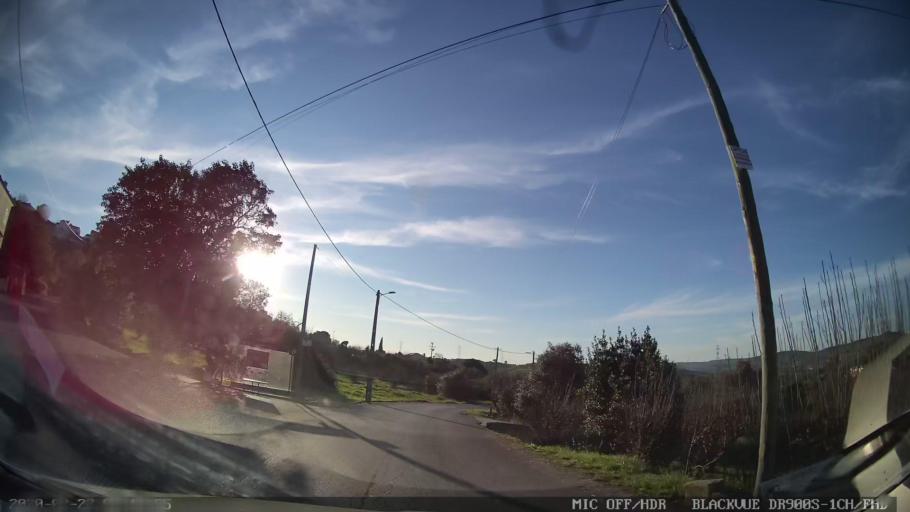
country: PT
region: Lisbon
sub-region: Vila Franca de Xira
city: Vila Franca de Xira
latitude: 38.9879
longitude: -9.0143
